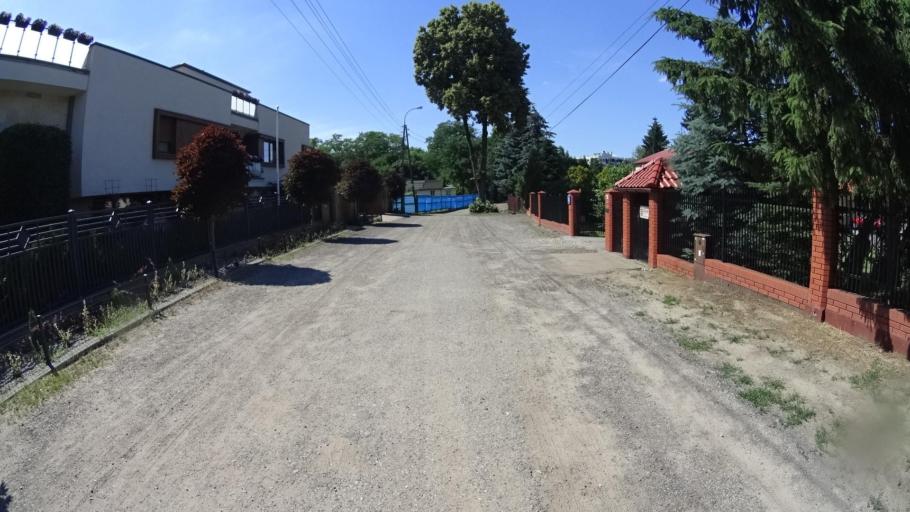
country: PL
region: Masovian Voivodeship
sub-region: Warszawa
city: Bialoleka
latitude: 52.3404
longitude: 20.9435
